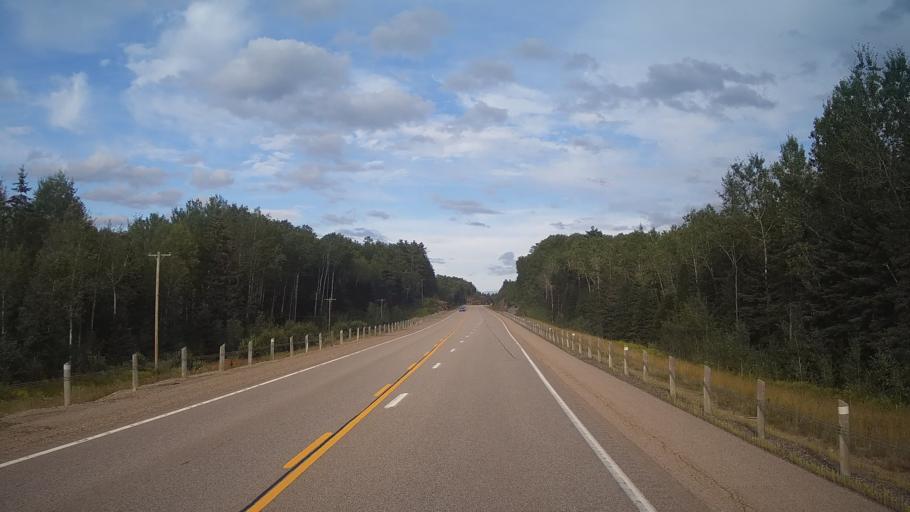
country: CA
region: Ontario
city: Mattawa
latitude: 46.2573
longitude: -78.2565
